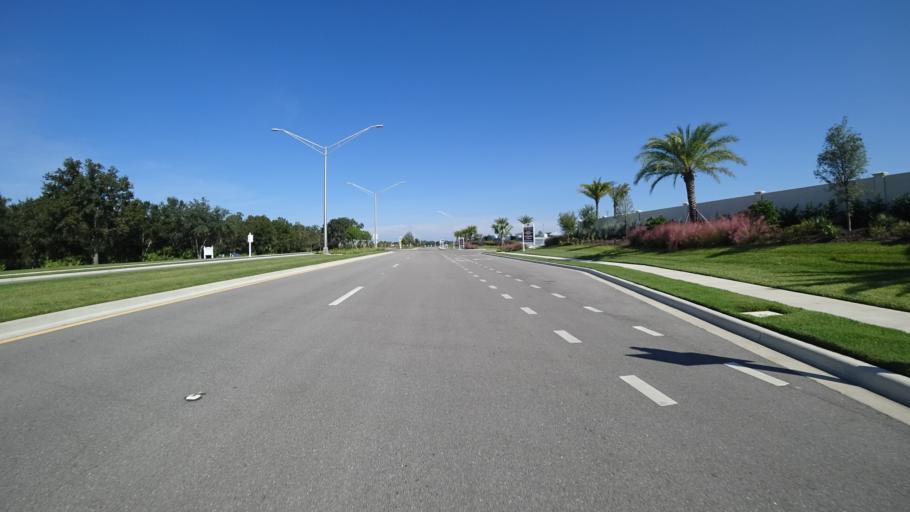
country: US
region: Florida
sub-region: Sarasota County
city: The Meadows
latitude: 27.4015
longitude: -82.3631
